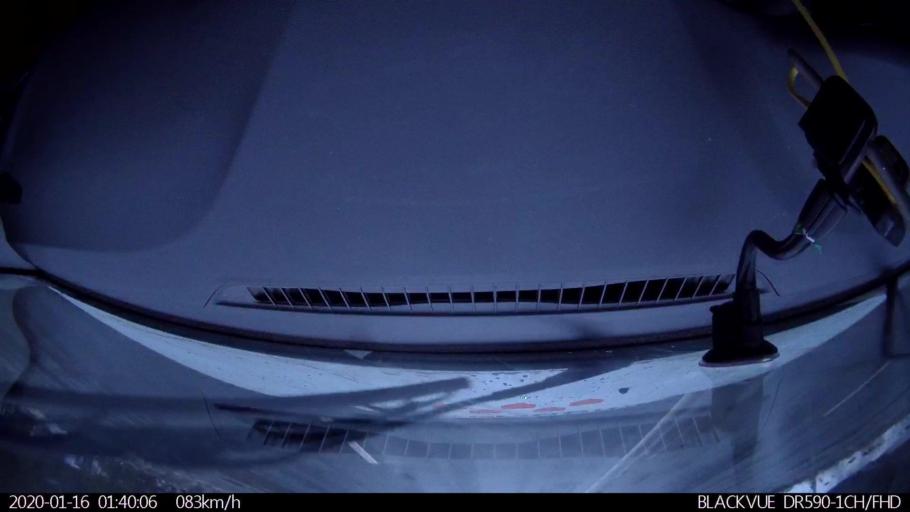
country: RU
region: Nizjnij Novgorod
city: Gorbatovka
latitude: 56.3291
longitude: 43.7841
